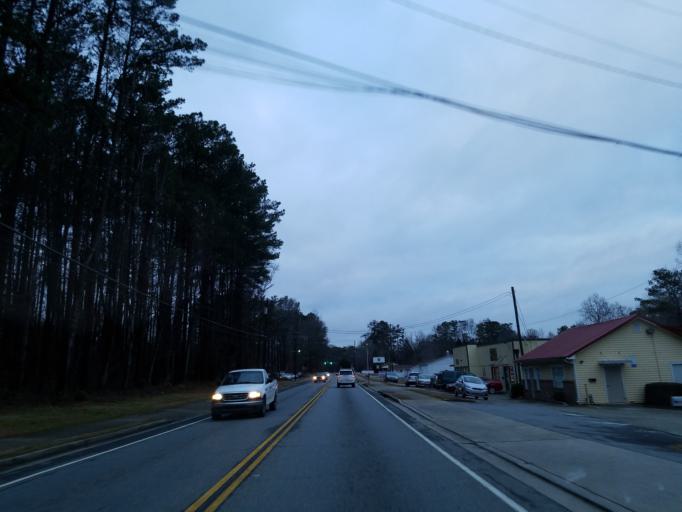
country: US
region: Georgia
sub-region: Cobb County
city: Acworth
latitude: 34.0560
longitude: -84.6639
